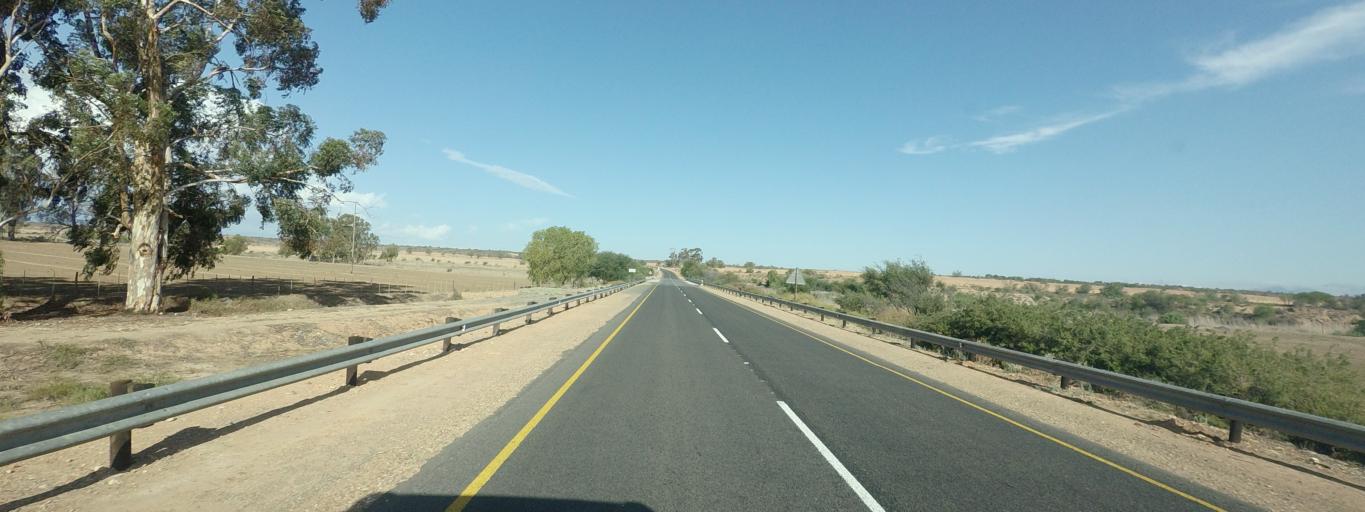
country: ZA
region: Western Cape
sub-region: Eden District Municipality
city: Oudtshoorn
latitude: -33.6024
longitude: 22.0585
